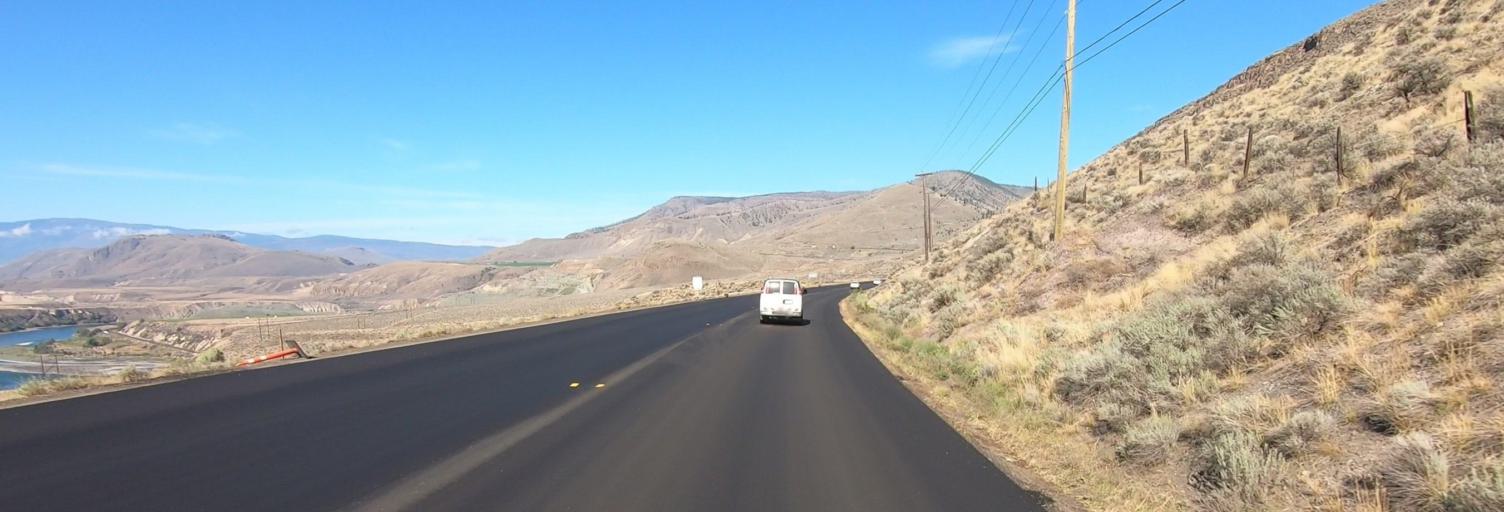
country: CA
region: British Columbia
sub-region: Thompson-Nicola Regional District
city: Ashcroft
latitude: 50.7913
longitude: -121.0840
